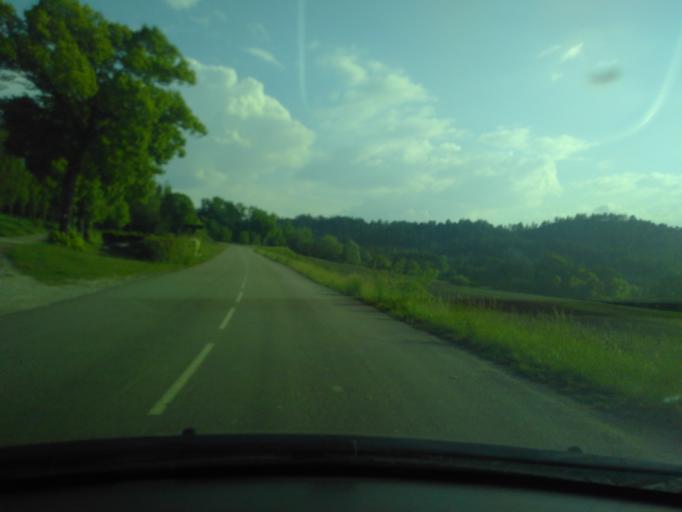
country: FR
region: Rhone-Alpes
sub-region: Departement de la Drome
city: Die
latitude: 44.6842
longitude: 5.4697
